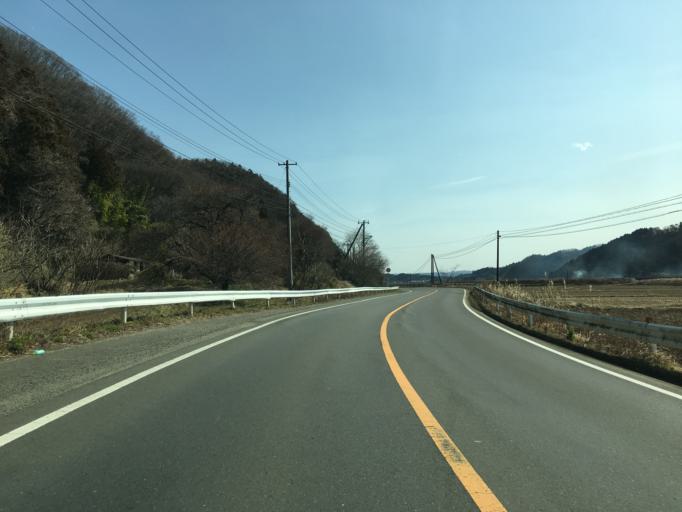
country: JP
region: Fukushima
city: Ishikawa
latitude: 37.1295
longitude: 140.2986
